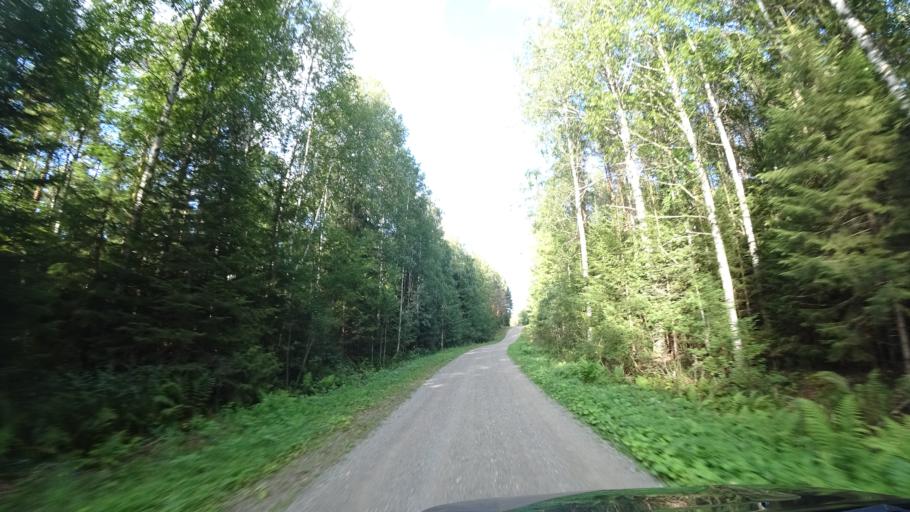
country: FI
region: Paijanne Tavastia
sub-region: Lahti
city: Auttoinen
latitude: 61.2211
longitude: 25.1828
